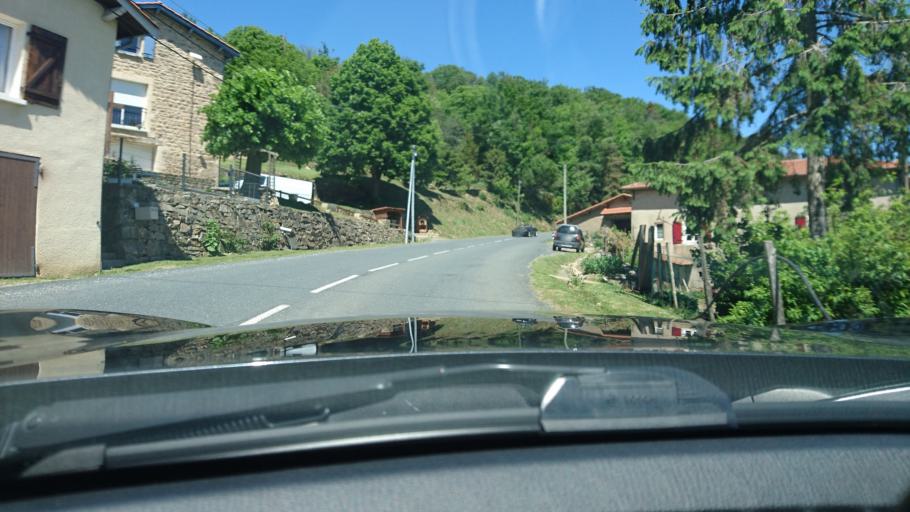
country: FR
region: Rhone-Alpes
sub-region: Departement du Rhone
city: Courzieu
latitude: 45.7163
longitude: 4.5877
